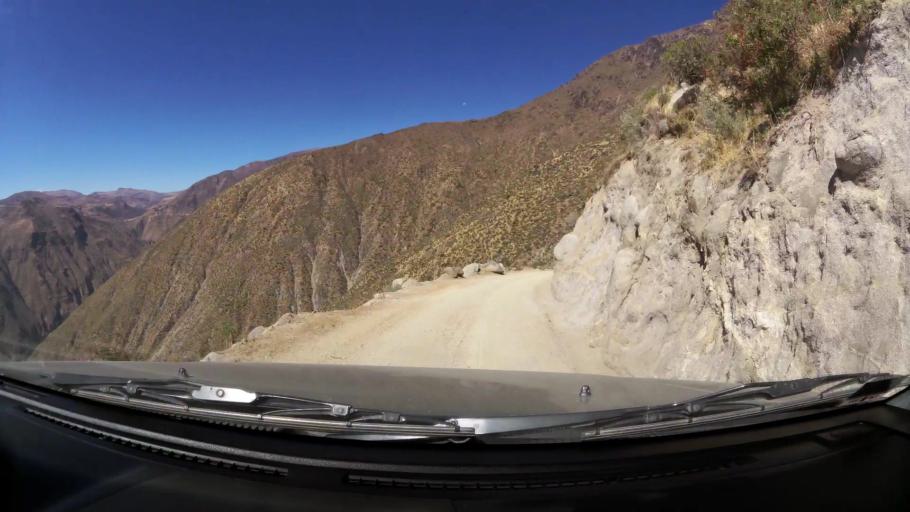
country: PE
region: Huancavelica
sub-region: Huaytara
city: Quito-Arma
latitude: -13.6167
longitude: -75.3520
